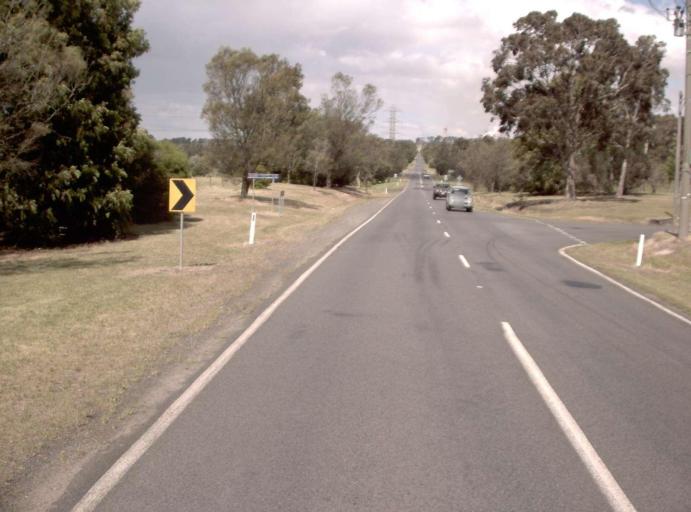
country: AU
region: Victoria
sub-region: Latrobe
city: Moe
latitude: -38.1719
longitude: 146.3016
